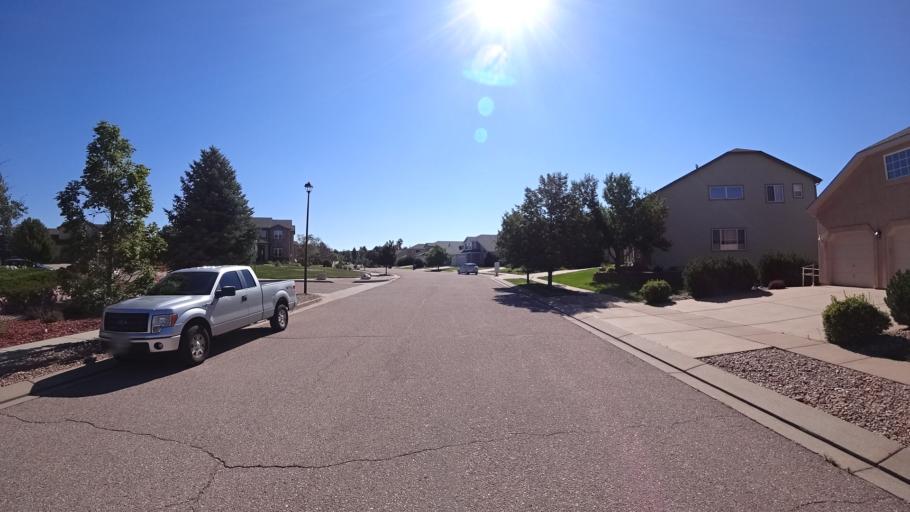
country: US
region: Colorado
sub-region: El Paso County
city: Gleneagle
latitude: 38.9751
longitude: -104.7831
